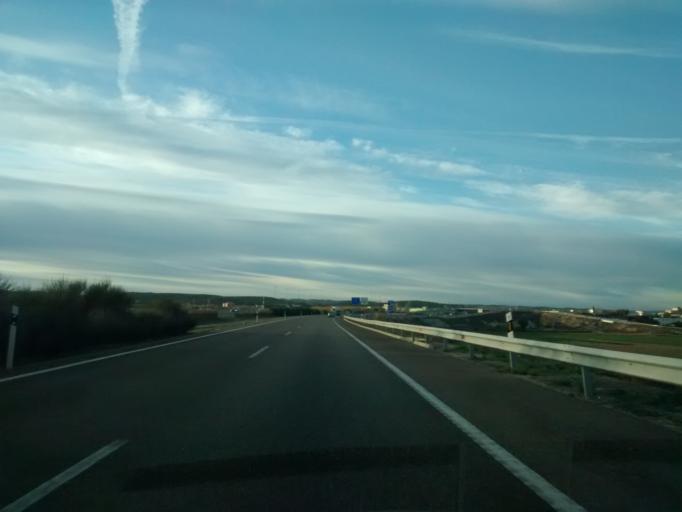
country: ES
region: Aragon
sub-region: Provincia de Zaragoza
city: Zaragoza
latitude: 41.7076
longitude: -0.8441
